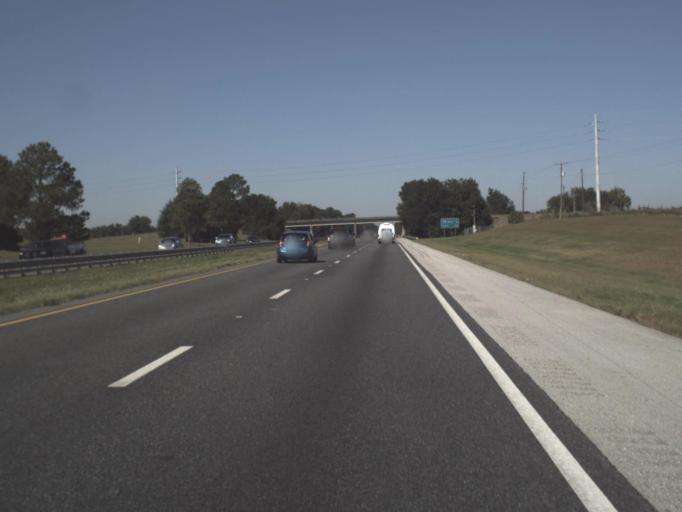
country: US
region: Florida
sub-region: Sumter County
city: Wildwood
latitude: 28.7973
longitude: -81.9965
